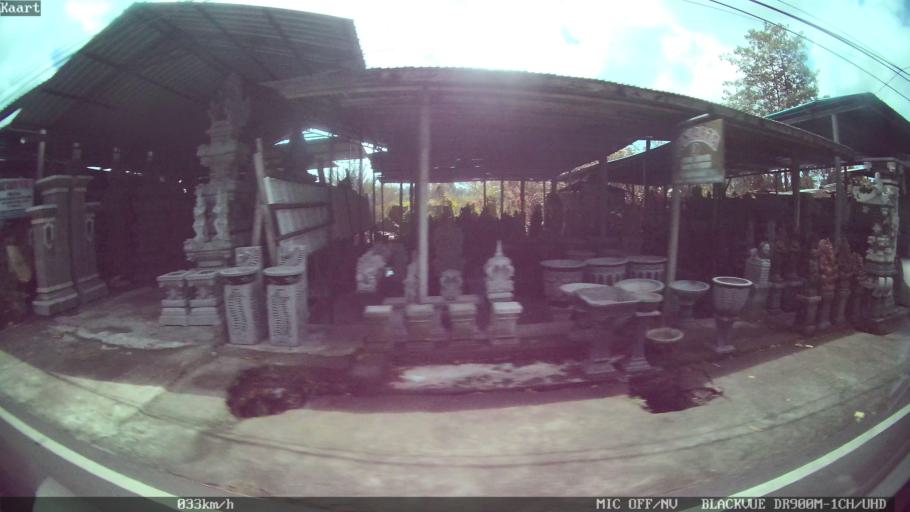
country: ID
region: Bali
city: Banjar Sedang
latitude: -8.5654
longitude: 115.2818
